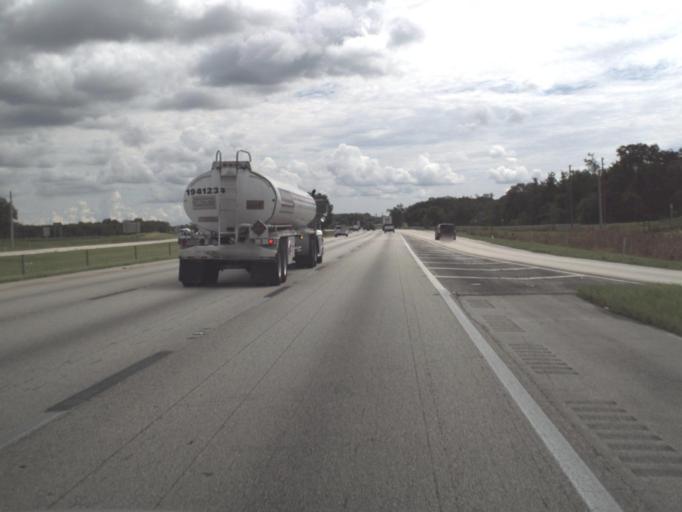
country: US
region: Florida
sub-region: Polk County
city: Polk City
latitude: 28.1574
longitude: -81.7988
